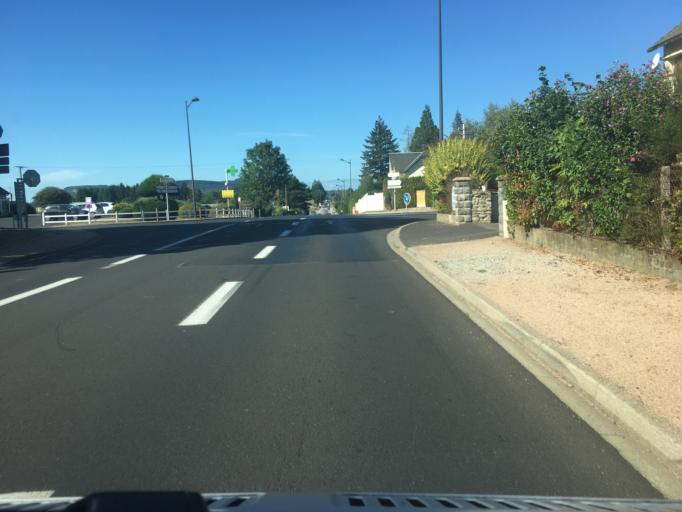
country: FR
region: Auvergne
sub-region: Departement du Cantal
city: Lanobre
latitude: 45.4396
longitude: 2.5281
